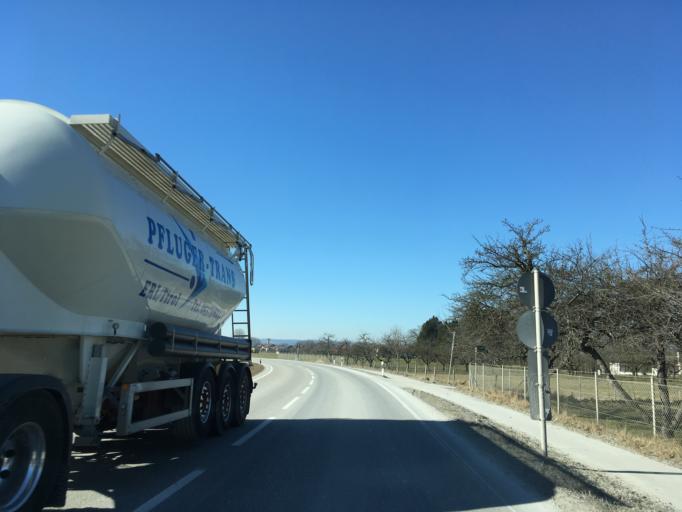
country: DE
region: Bavaria
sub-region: Upper Bavaria
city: Rohrdorf
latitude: 47.7937
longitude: 12.1789
